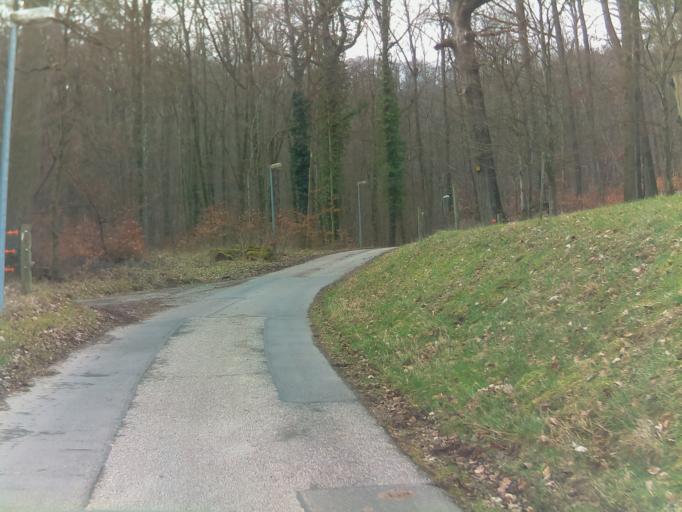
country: DE
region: Baden-Wuerttemberg
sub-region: Regierungsbezirk Stuttgart
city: Sersheim
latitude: 49.0043
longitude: 9.0024
